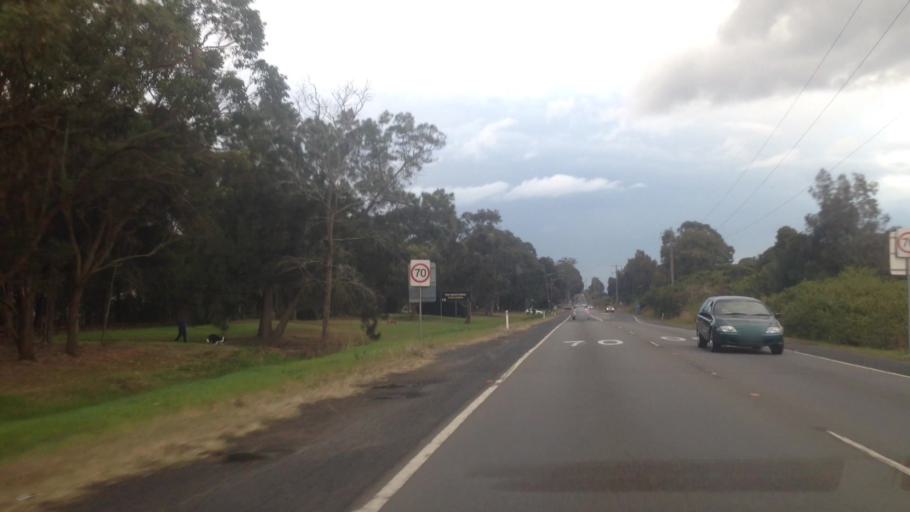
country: AU
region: New South Wales
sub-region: Wyong Shire
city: Chittaway Bay
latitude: -33.2784
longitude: 151.4277
